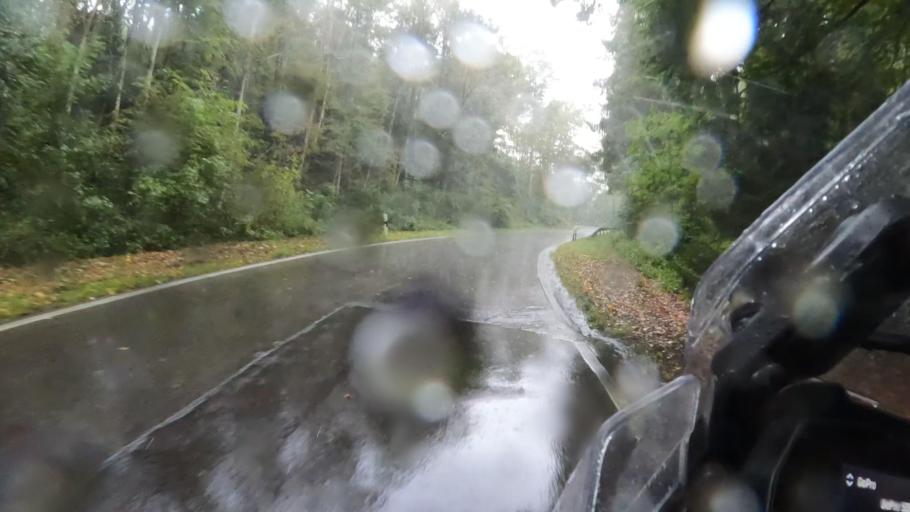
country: DE
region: Baden-Wuerttemberg
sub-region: Freiburg Region
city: Jestetten
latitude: 47.6447
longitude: 8.5861
